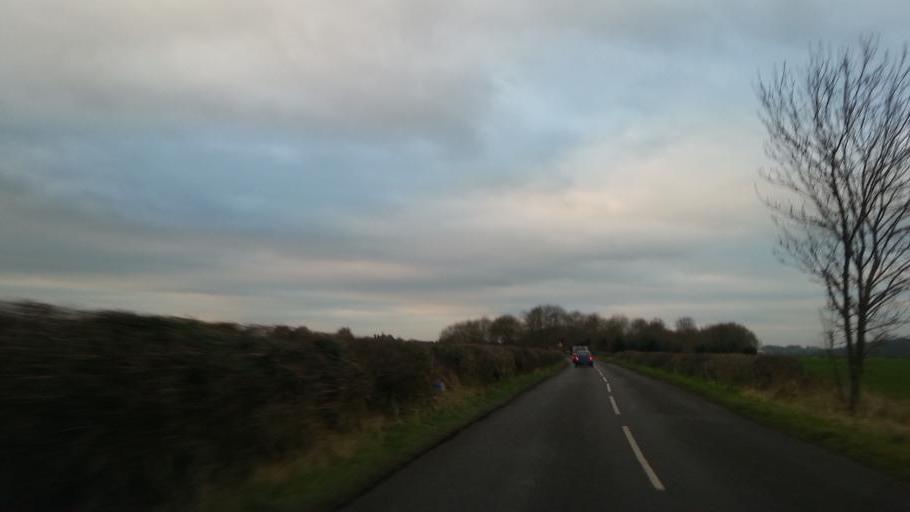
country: GB
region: England
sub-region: Nottinghamshire
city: Newark on Trent
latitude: 53.1017
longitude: -0.8287
